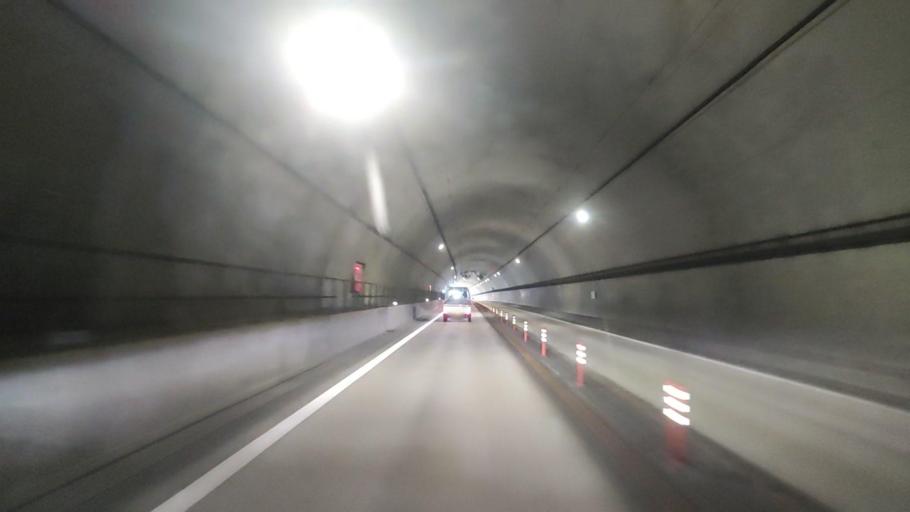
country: JP
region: Wakayama
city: Tanabe
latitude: 33.6297
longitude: 135.4146
